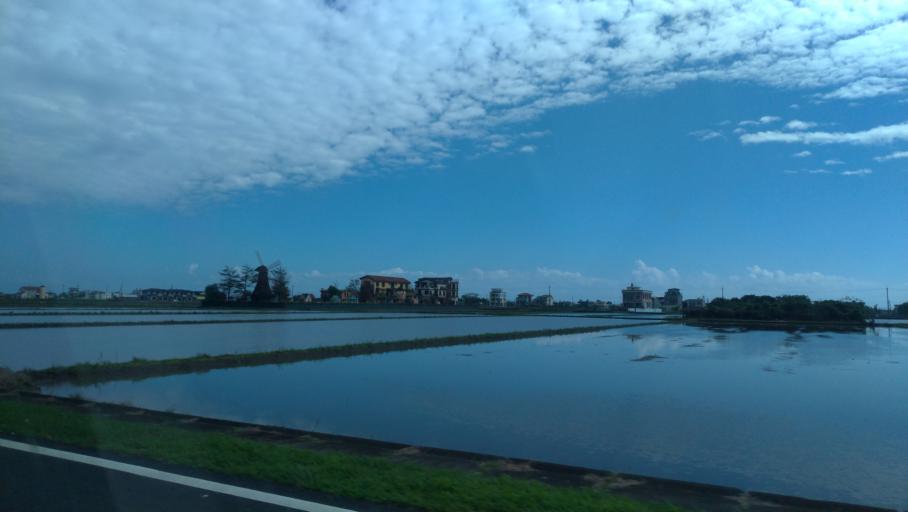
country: TW
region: Taiwan
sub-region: Yilan
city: Yilan
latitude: 24.7995
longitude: 121.7874
